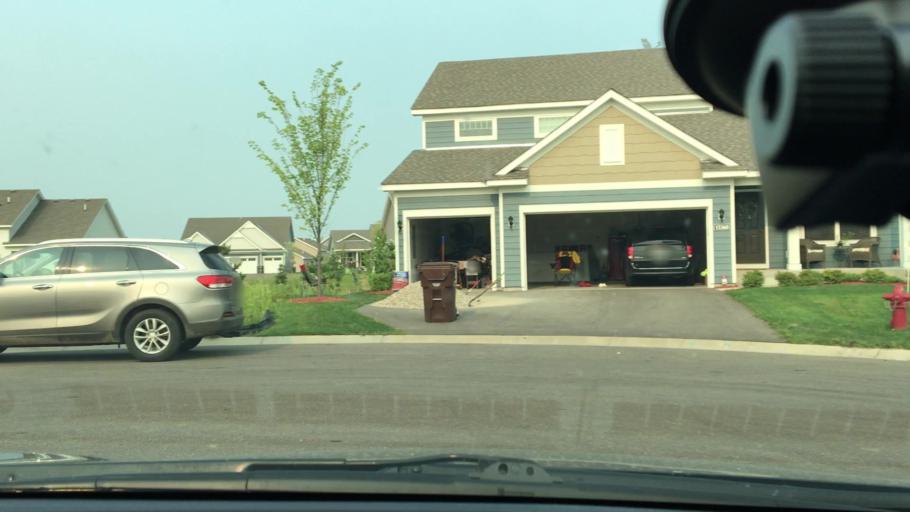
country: US
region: Minnesota
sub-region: Hennepin County
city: Champlin
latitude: 45.1970
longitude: -93.4363
